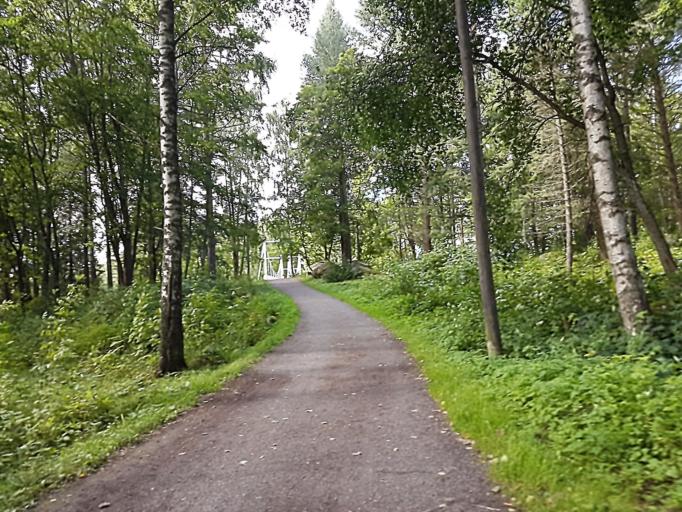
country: FI
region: Pirkanmaa
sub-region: Etelae-Pirkanmaa
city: Valkeakoski
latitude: 61.2714
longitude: 24.0512
